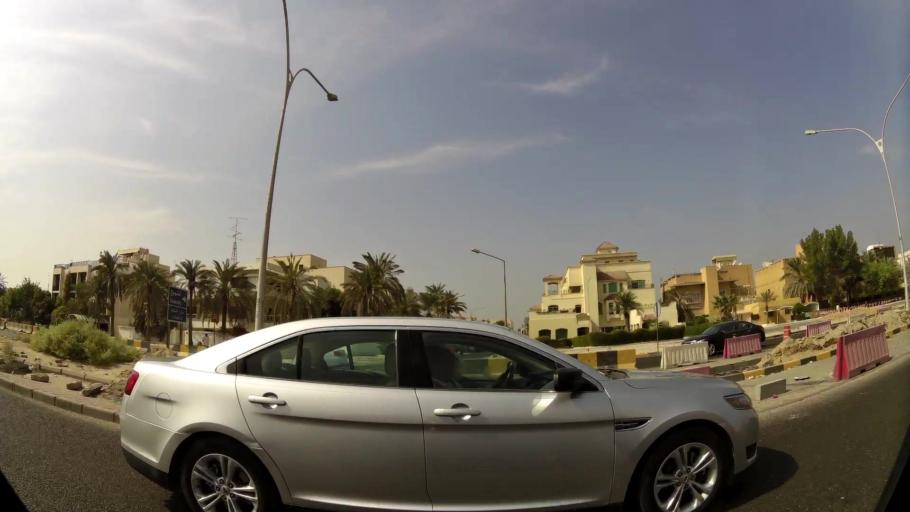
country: KW
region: Al Asimah
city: Ash Shamiyah
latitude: 29.3530
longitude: 47.9599
